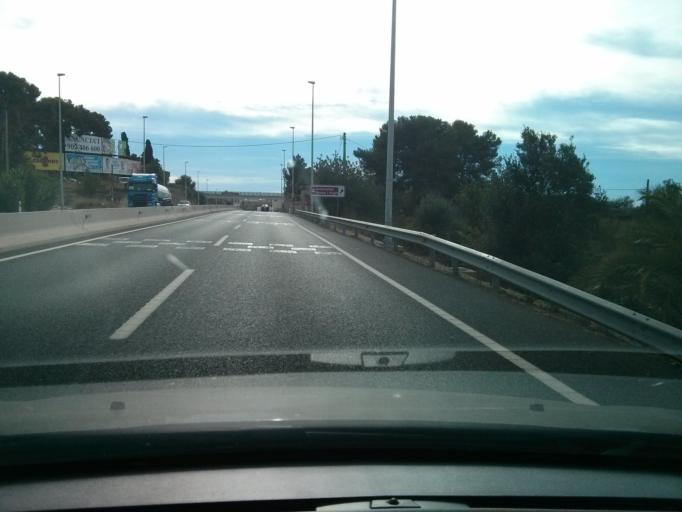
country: ES
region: Catalonia
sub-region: Provincia de Tarragona
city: Tarragona
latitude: 41.1332
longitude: 1.2390
